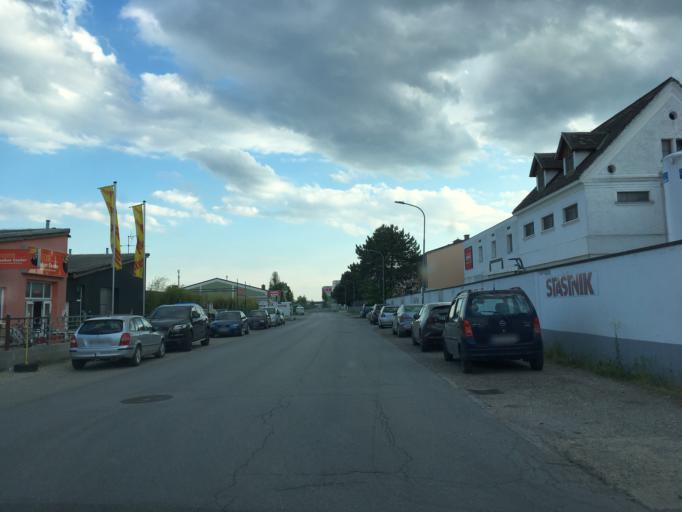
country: AT
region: Lower Austria
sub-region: Politischer Bezirk Wien-Umgebung
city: Gerasdorf bei Wien
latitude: 48.2836
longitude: 16.4816
